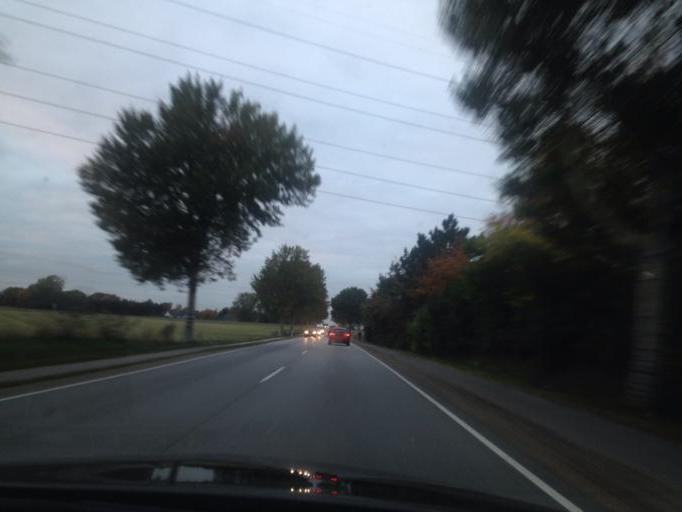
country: DK
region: Zealand
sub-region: Solrod Kommune
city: Solrod
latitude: 55.5484
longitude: 12.1667
